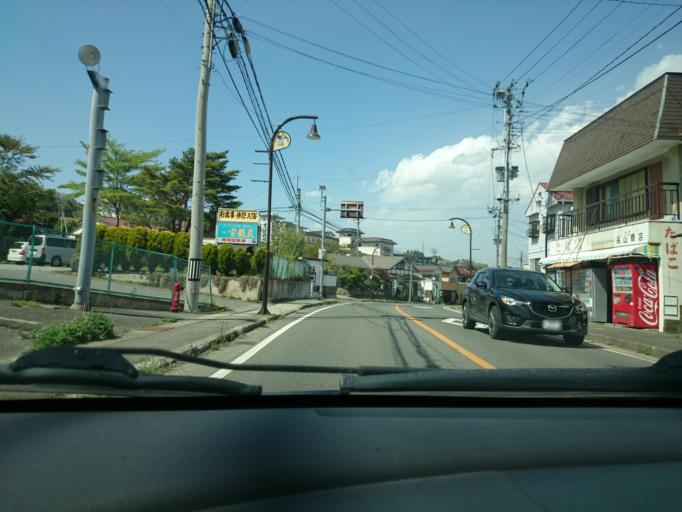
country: JP
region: Fukushima
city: Nihommatsu
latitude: 37.6044
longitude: 140.3564
